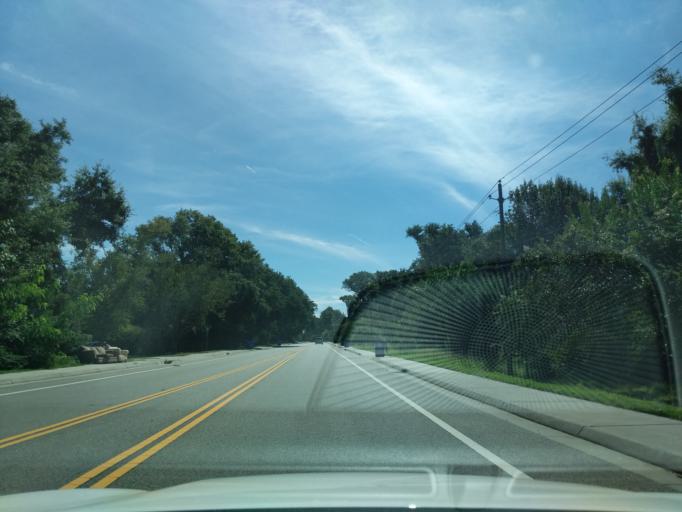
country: US
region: South Carolina
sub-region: Charleston County
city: Charleston
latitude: 32.7420
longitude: -79.9274
